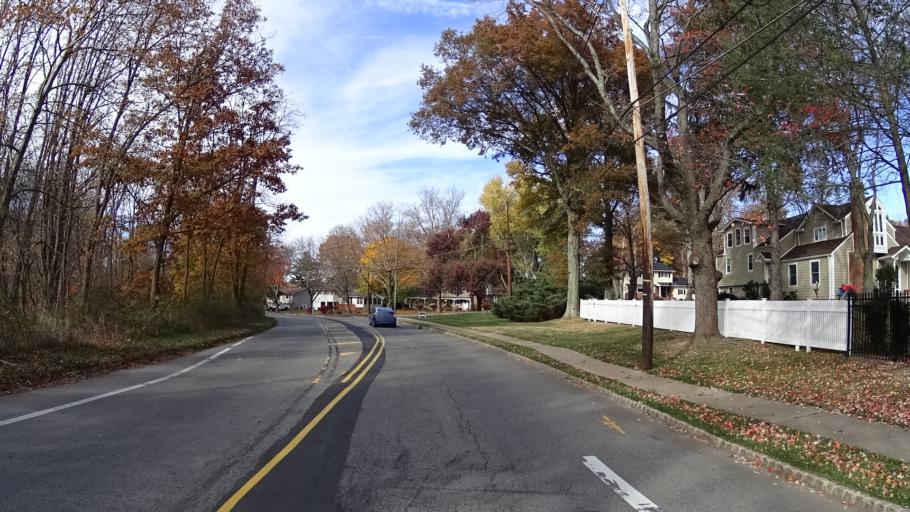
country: US
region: New Jersey
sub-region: Morris County
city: Madison
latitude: 40.7349
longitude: -74.4193
